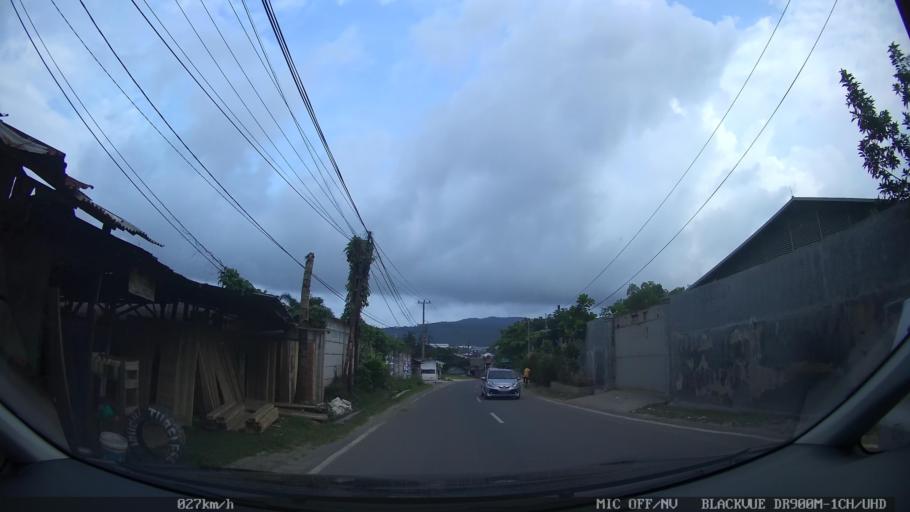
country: ID
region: Lampung
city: Bandarlampung
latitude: -5.4062
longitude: 105.2914
